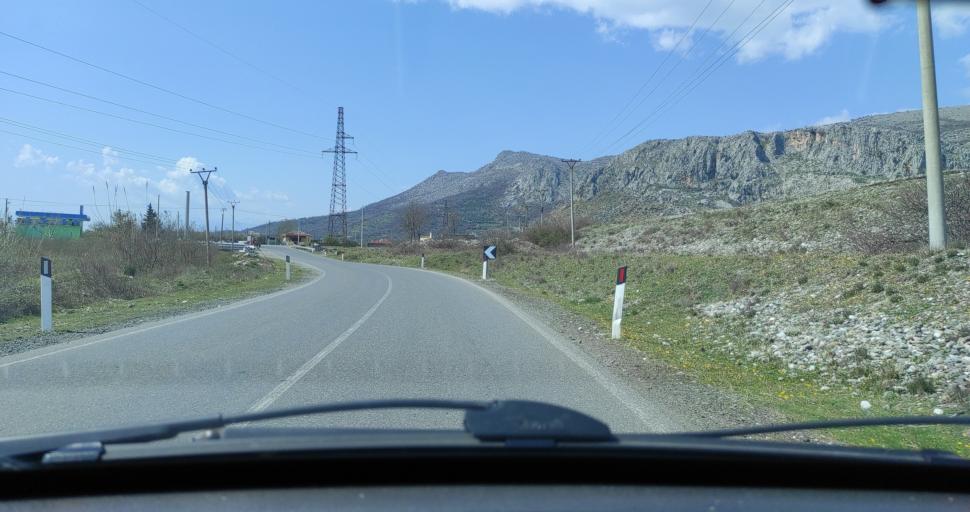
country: AL
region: Shkoder
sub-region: Rrethi i Shkodres
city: Vau i Dejes
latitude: 42.0061
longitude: 19.6205
